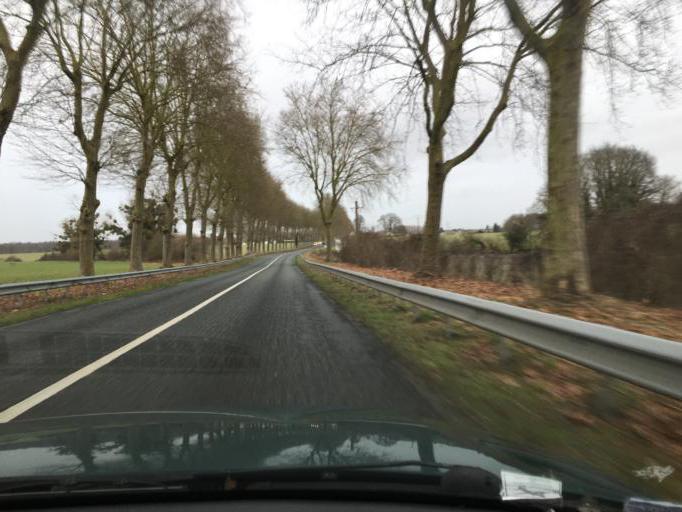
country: FR
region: Picardie
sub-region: Departement de l'Oise
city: La Chapelle-en-Serval
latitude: 49.1444
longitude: 2.5415
